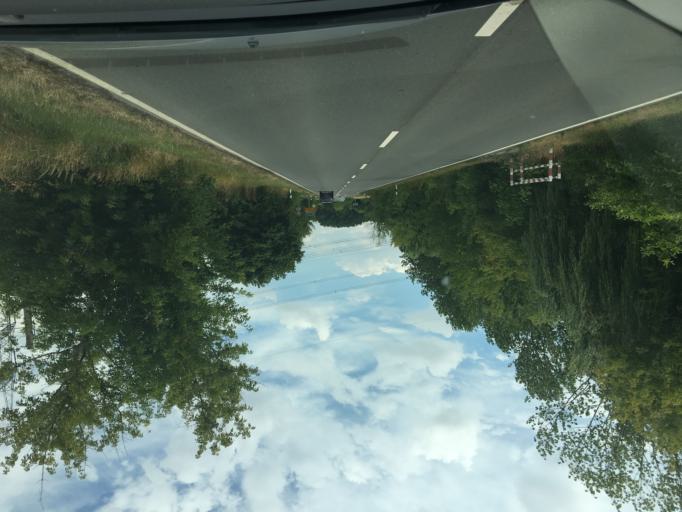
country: DE
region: Saxony-Anhalt
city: Holleben
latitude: 51.4216
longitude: 11.9309
